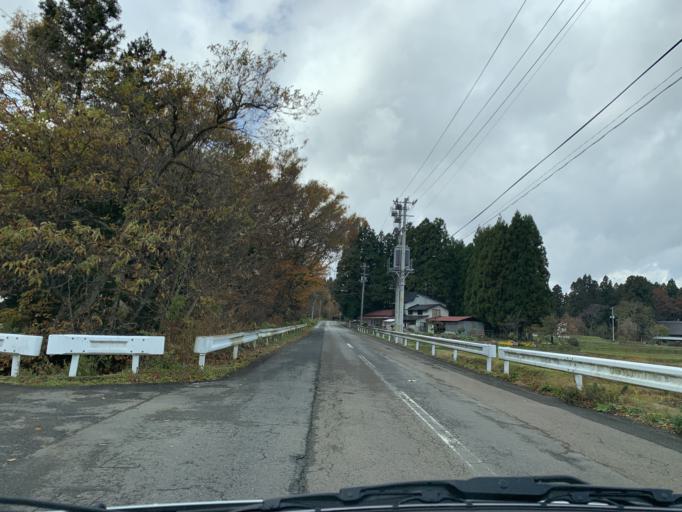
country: JP
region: Iwate
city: Mizusawa
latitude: 39.0789
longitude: 141.0419
